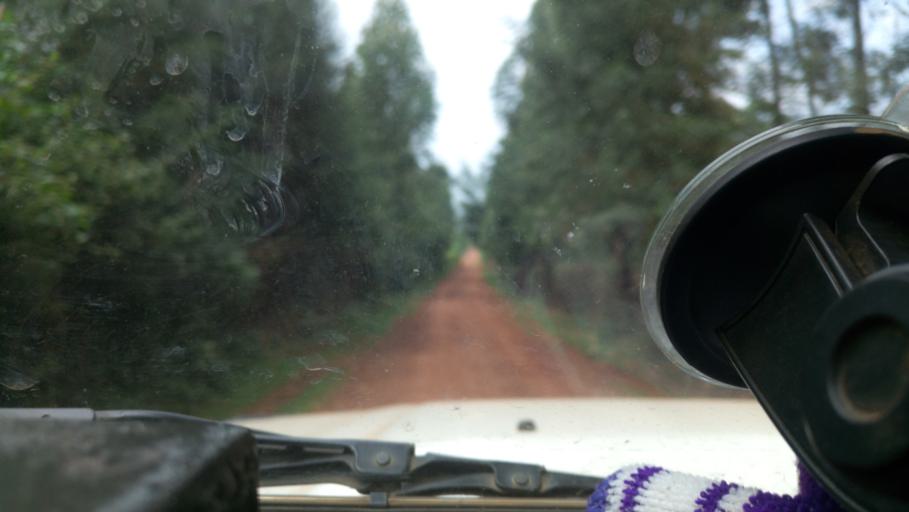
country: KE
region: Kericho
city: Litein
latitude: -0.6296
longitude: 35.1865
